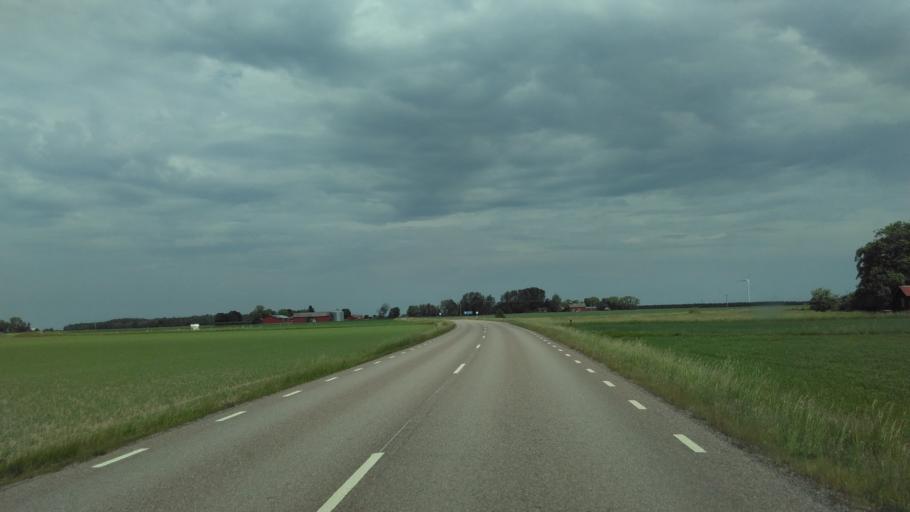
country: SE
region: Vaestra Goetaland
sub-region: Vara Kommun
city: Kvanum
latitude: 58.3392
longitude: 13.1267
